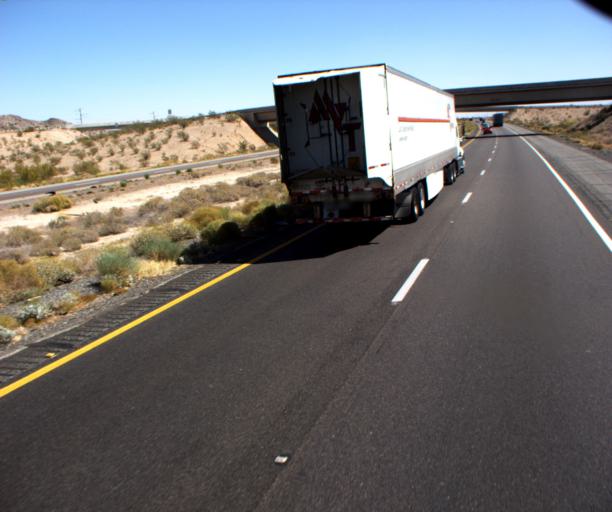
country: US
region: Arizona
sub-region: Maricopa County
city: Buckeye
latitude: 33.4278
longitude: -112.6273
